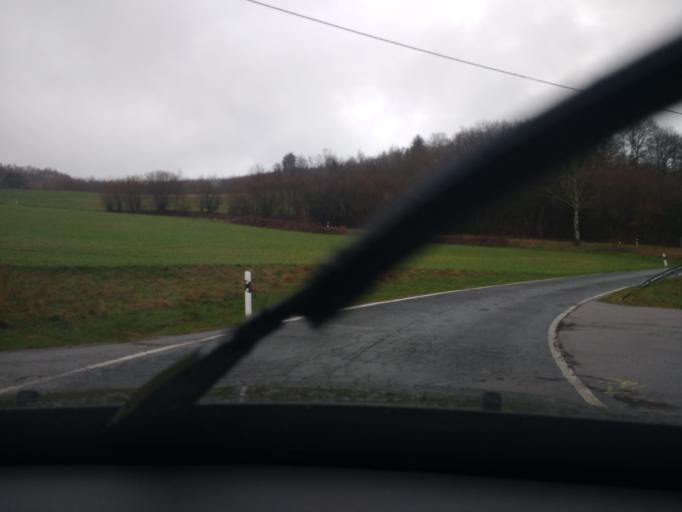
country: DE
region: Rheinland-Pfalz
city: Lampaden
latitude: 49.6430
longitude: 6.7074
